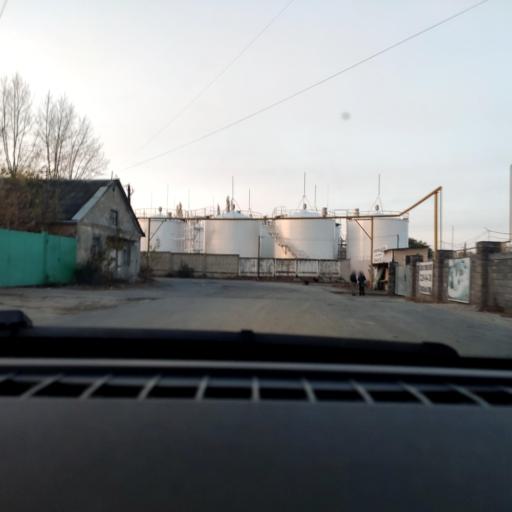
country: RU
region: Voronezj
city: Voronezh
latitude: 51.6490
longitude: 39.2770
